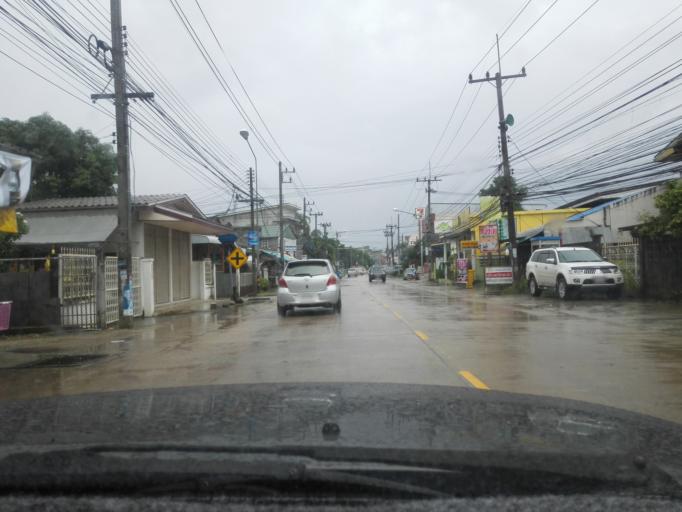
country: TH
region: Tak
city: Mae Sot
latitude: 16.7182
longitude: 98.5863
